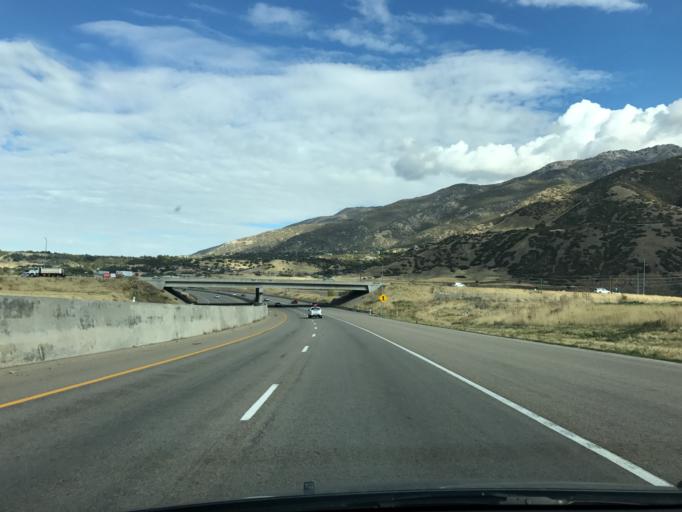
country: US
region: Utah
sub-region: Davis County
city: South Weber
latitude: 41.1265
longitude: -111.9078
